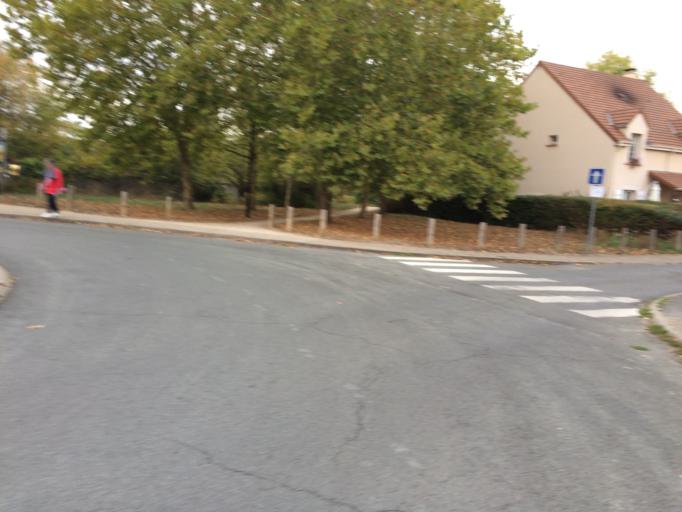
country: FR
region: Ile-de-France
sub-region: Departement de l'Essonne
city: Marcoussis
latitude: 48.6398
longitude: 2.2334
